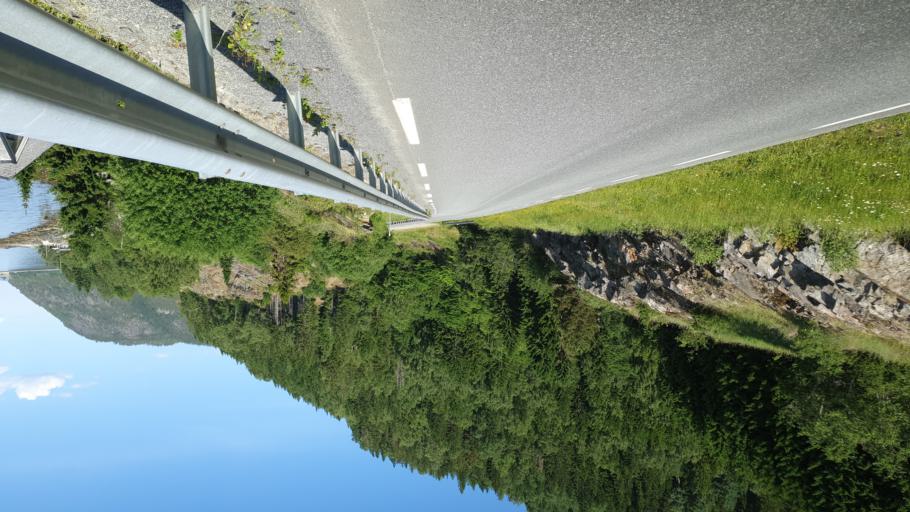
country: NO
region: Nord-Trondelag
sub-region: Leksvik
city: Leksvik
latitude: 63.6129
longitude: 10.5086
